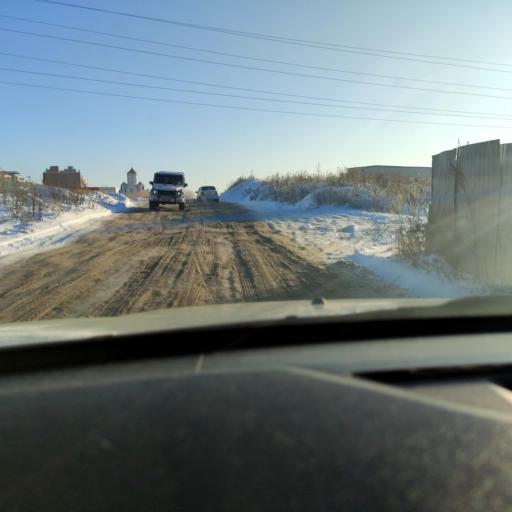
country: RU
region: Samara
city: Petra-Dubrava
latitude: 53.3193
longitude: 50.3017
